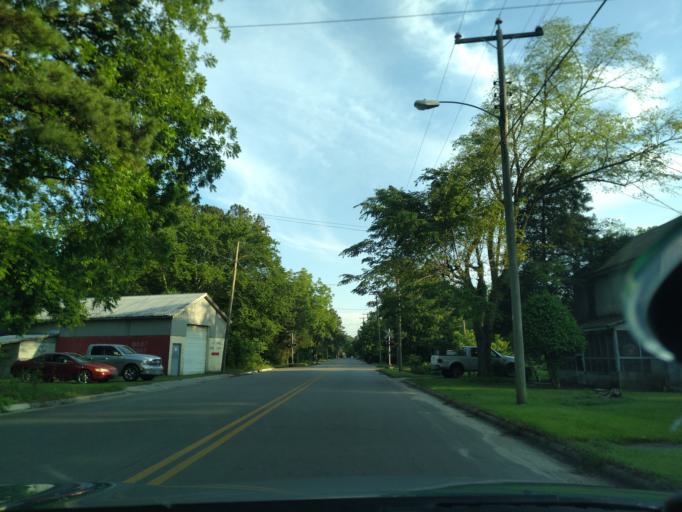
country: US
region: North Carolina
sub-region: Washington County
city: Plymouth
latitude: 35.8613
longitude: -76.7537
